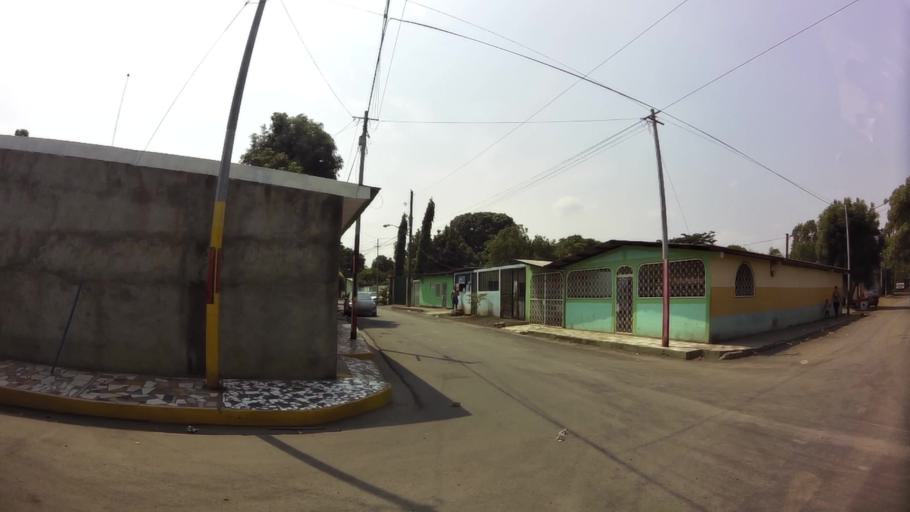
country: NI
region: Managua
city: Ciudad Sandino
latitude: 12.1264
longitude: -86.3146
